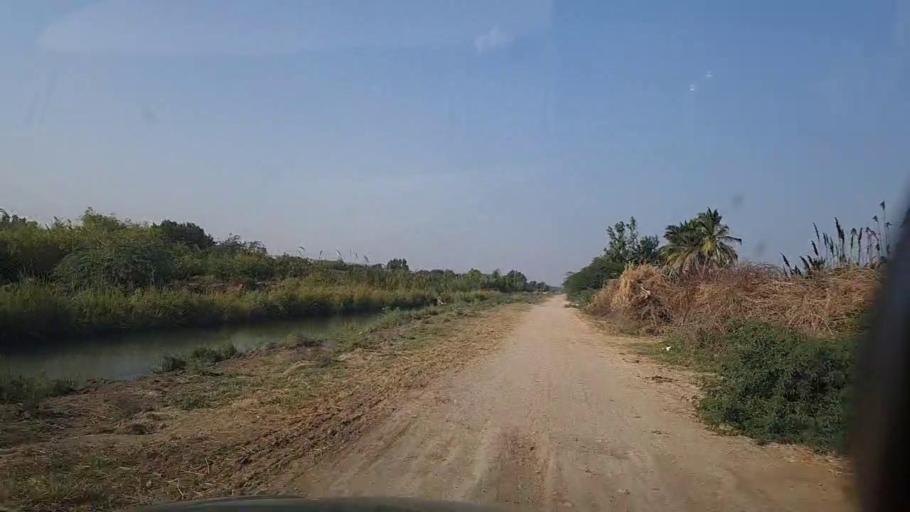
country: PK
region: Sindh
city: Thatta
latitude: 24.6099
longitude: 67.8764
